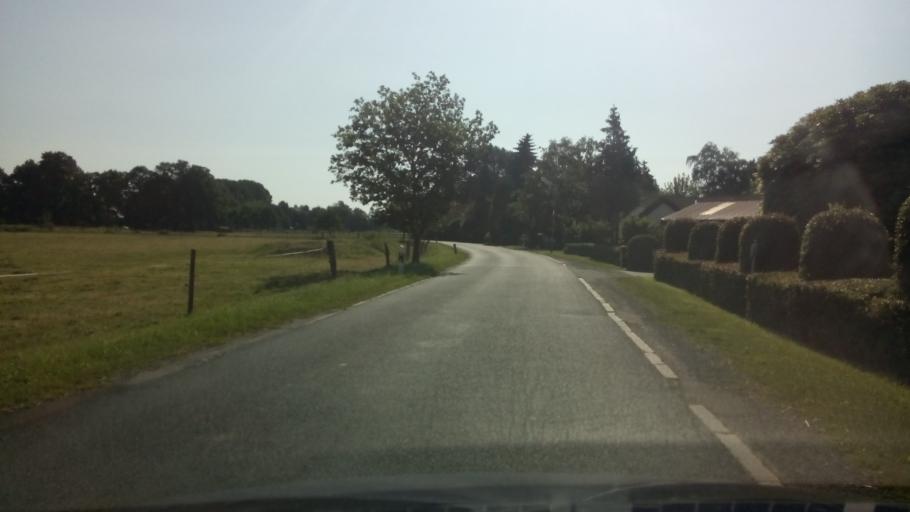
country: DE
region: Lower Saxony
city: Lilienthal
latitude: 53.1430
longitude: 8.9483
